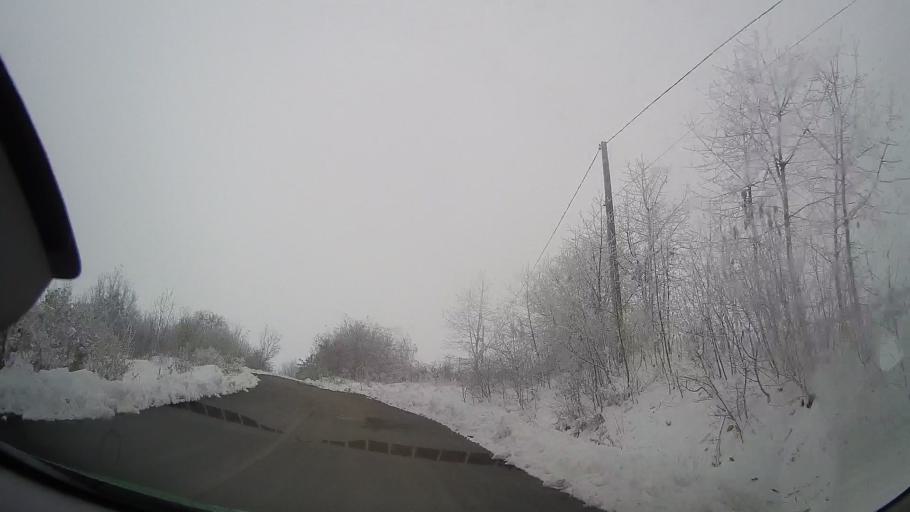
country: RO
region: Iasi
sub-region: Comuna Tansa
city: Suhulet
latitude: 46.8921
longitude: 27.2787
